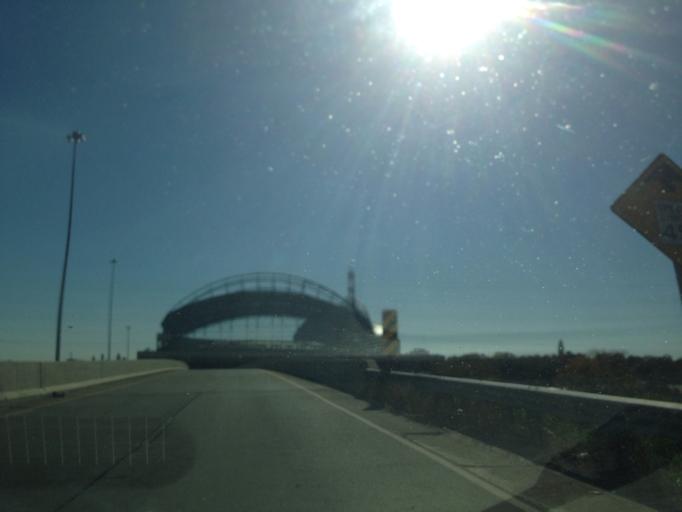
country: US
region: Wisconsin
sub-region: Milwaukee County
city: West Milwaukee
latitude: 43.0341
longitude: -87.9707
